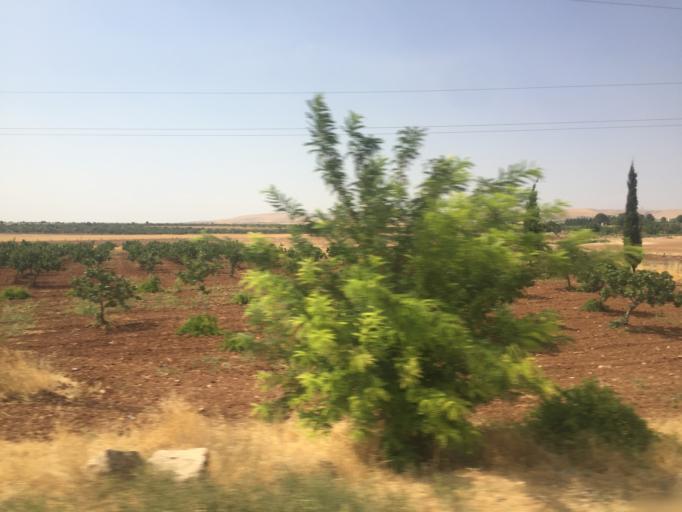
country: TR
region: Sanliurfa
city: Akziyaret
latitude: 37.3820
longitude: 38.8506
